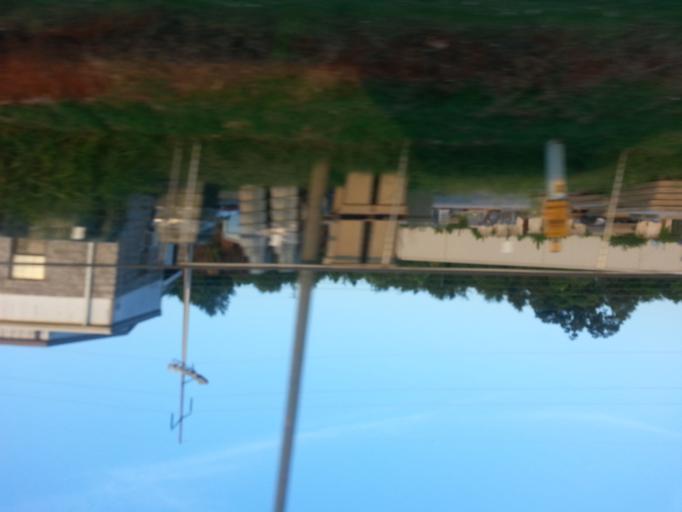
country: US
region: Tennessee
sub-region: Monroe County
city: Sweetwater
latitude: 35.6351
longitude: -84.4371
